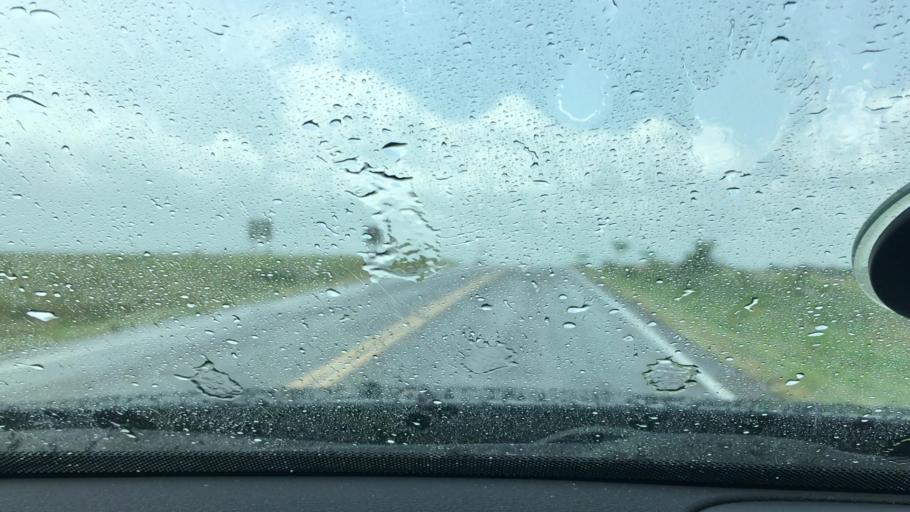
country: US
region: Oklahoma
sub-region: Johnston County
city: Tishomingo
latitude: 34.1722
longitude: -96.7132
